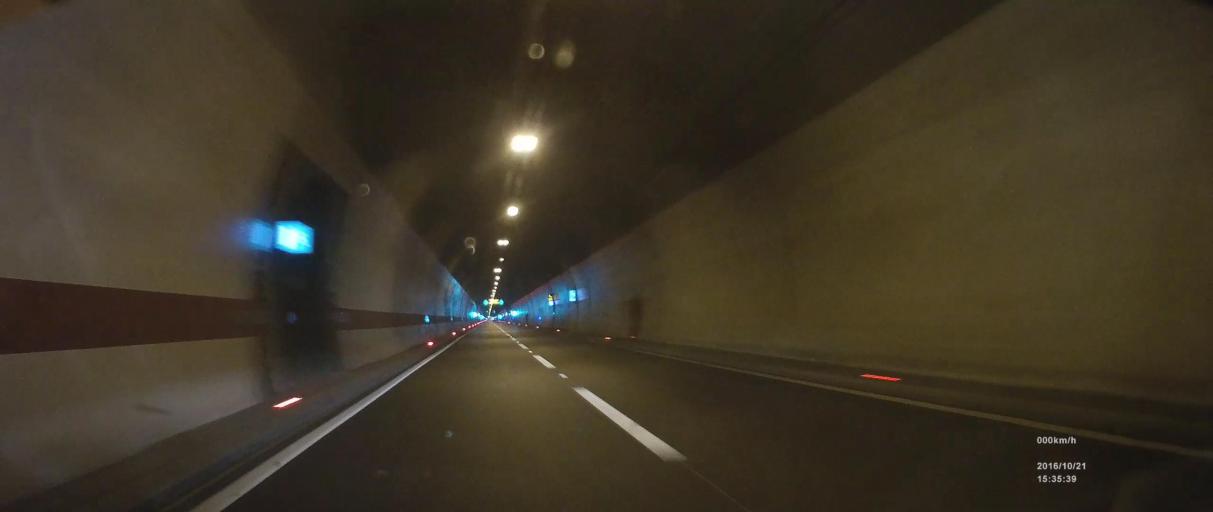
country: HR
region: Zadarska
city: Obrovac
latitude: 44.2612
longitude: 15.6535
